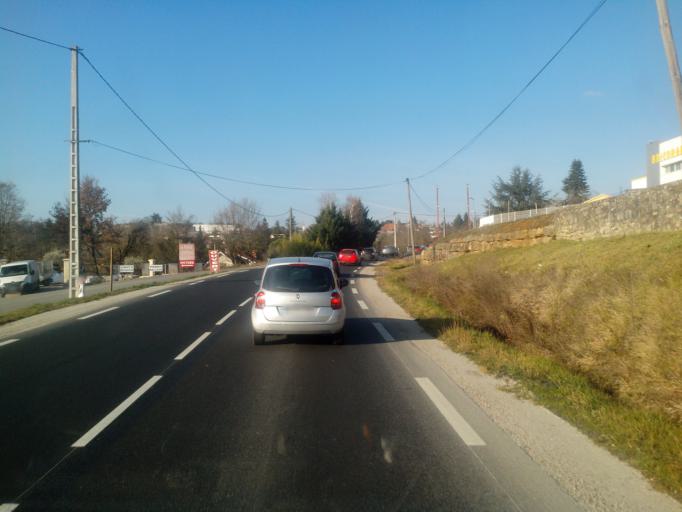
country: FR
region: Midi-Pyrenees
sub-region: Departement de l'Aveyron
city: Capdenac-Gare
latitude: 44.5904
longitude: 2.0657
